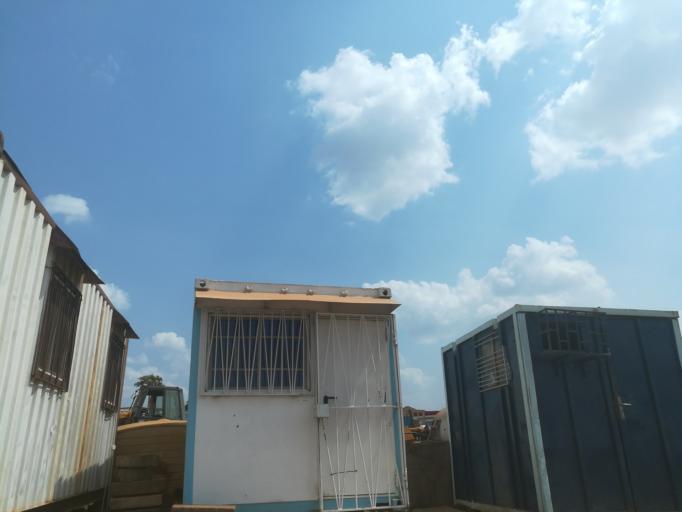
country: NG
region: Abuja Federal Capital Territory
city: Abuja
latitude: 9.0601
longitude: 7.4454
